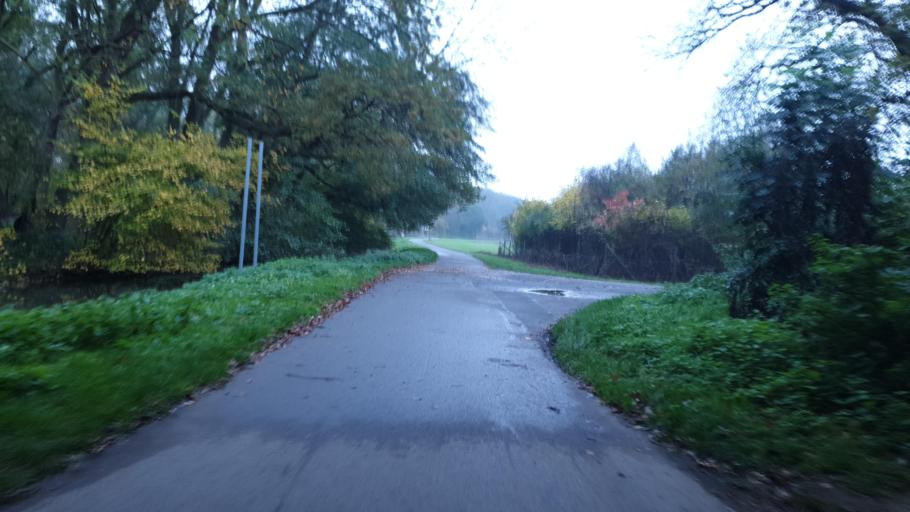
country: DE
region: North Rhine-Westphalia
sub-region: Regierungsbezirk Koln
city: Kerpen
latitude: 50.9094
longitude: 6.6956
